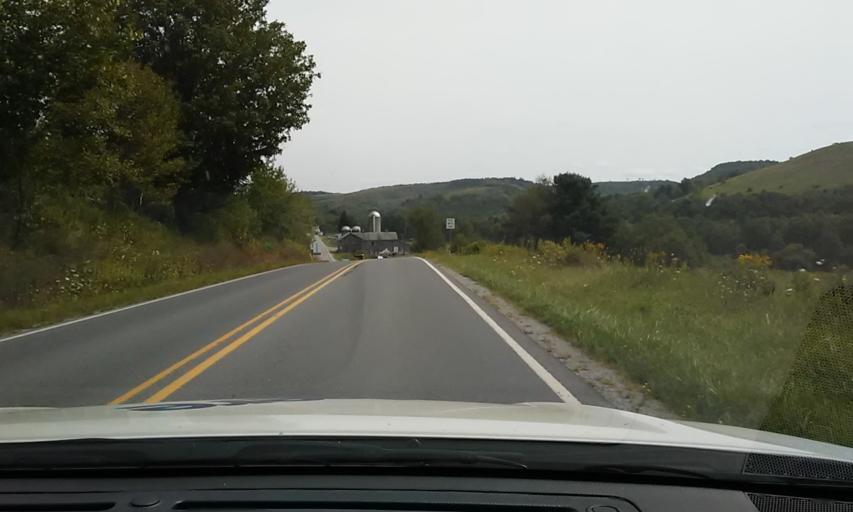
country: US
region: Pennsylvania
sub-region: Elk County
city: Ridgway
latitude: 41.3140
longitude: -78.6506
